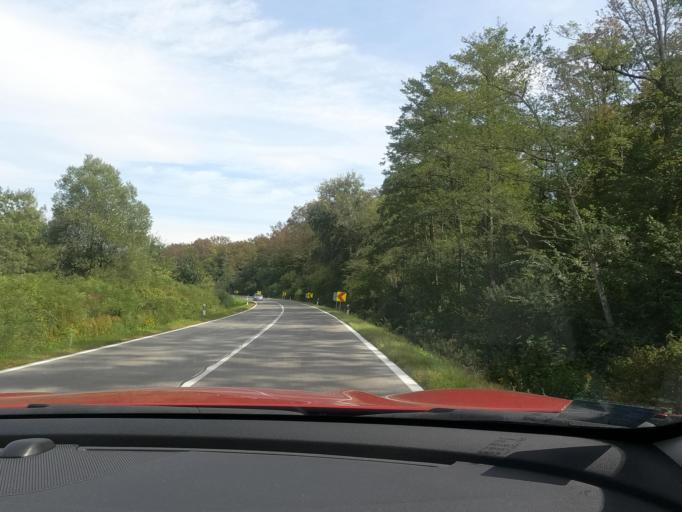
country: HR
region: Sisacko-Moslavacka
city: Osekovo
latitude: 45.5071
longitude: 16.5250
